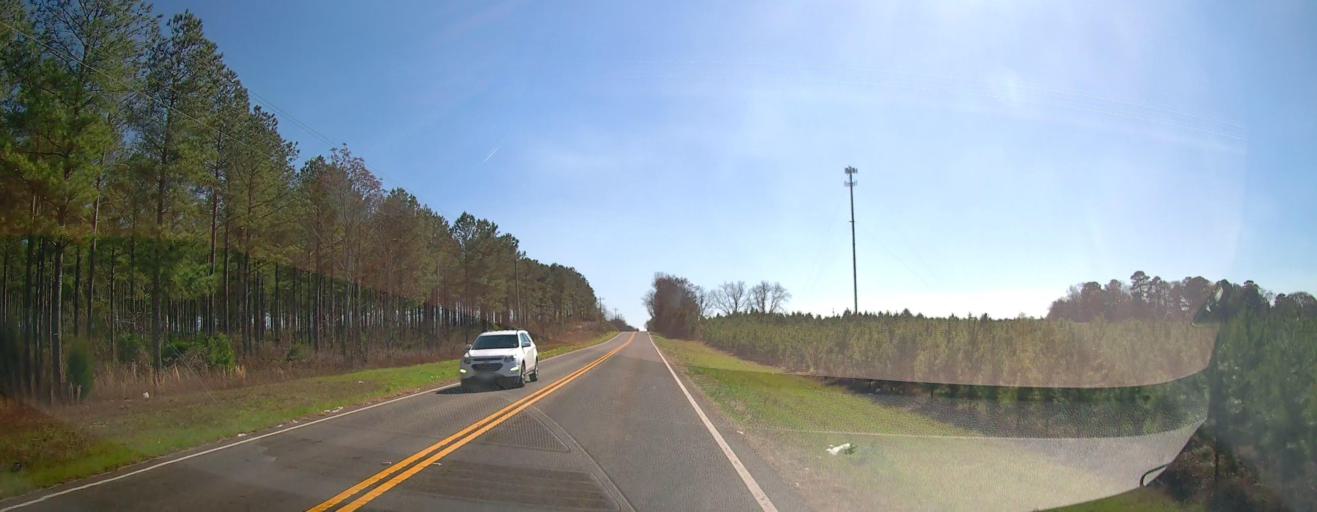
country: US
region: Georgia
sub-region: Macon County
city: Montezuma
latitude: 32.3480
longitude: -84.0191
